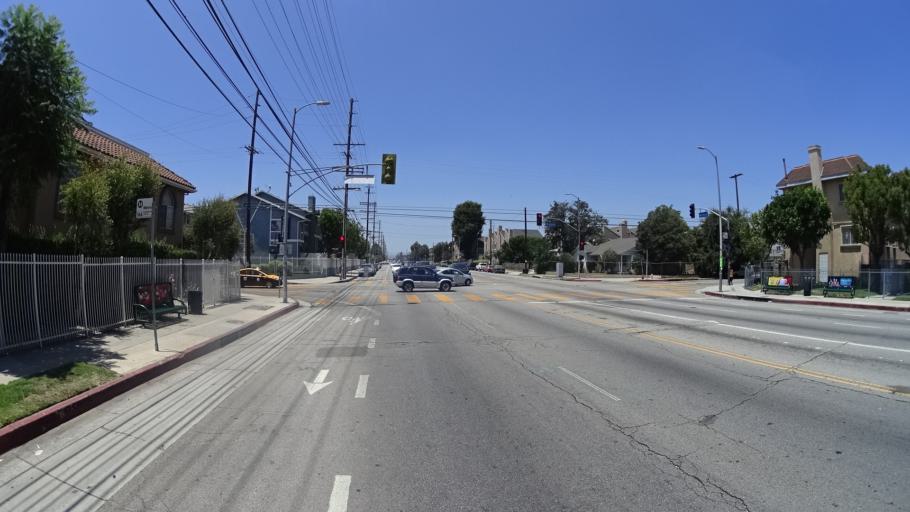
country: US
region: California
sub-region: Los Angeles County
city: Van Nuys
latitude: 34.2354
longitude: -118.4608
